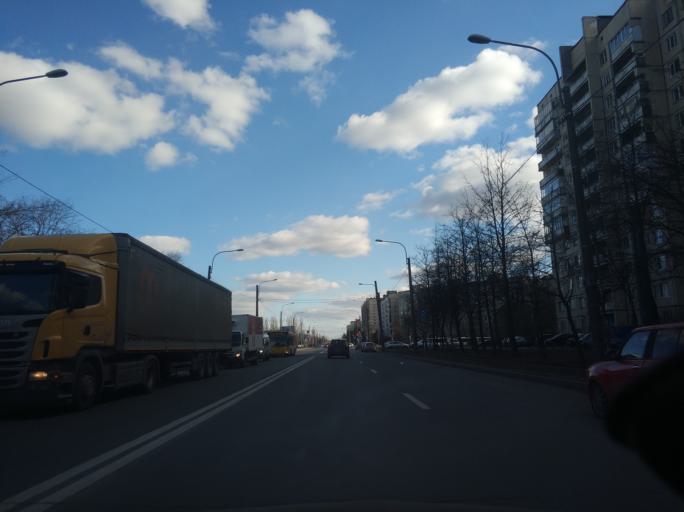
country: RU
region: St.-Petersburg
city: Krasnogvargeisky
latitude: 59.9585
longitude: 30.4921
